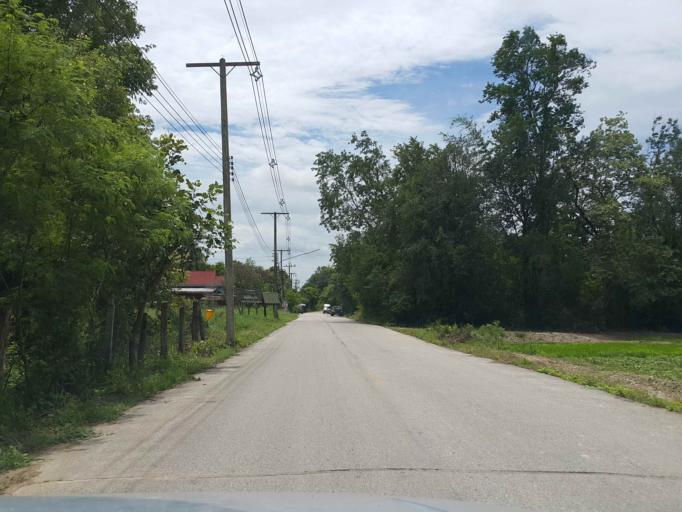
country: TH
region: Sukhothai
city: Ban Na
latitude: 17.0100
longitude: 99.7062
